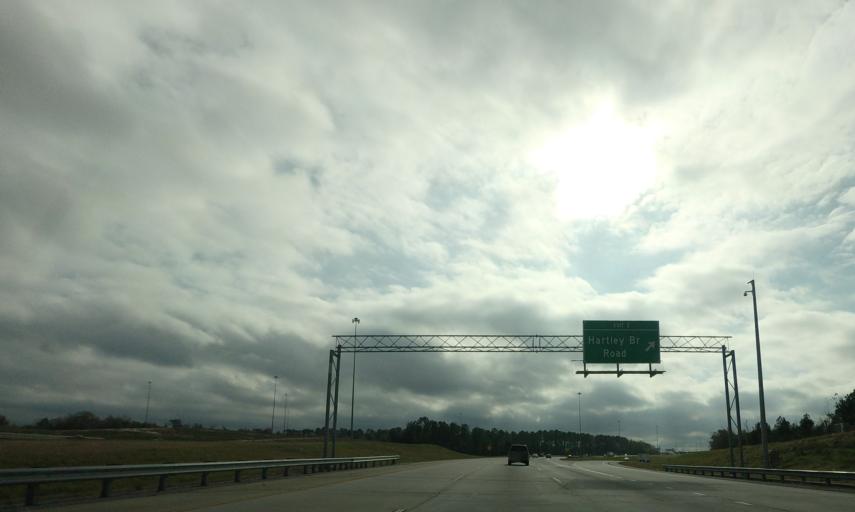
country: US
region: Georgia
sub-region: Bibb County
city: West Point
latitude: 32.7583
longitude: -83.7111
